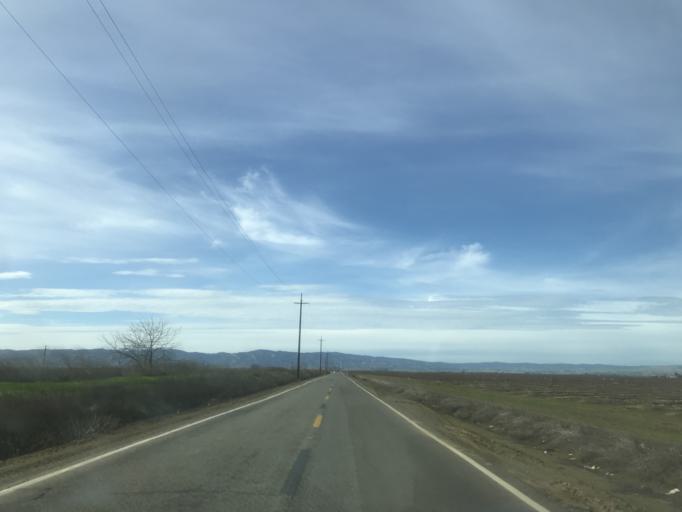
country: US
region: California
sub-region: Yolo County
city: Cottonwood
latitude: 38.6637
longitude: -121.8975
